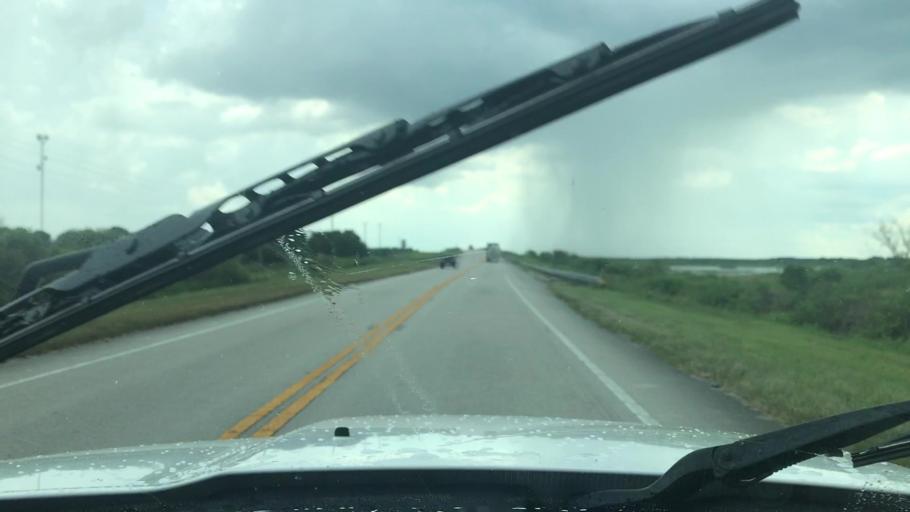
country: US
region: Florida
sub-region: Polk County
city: Babson Park
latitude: 27.8046
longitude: -81.1920
